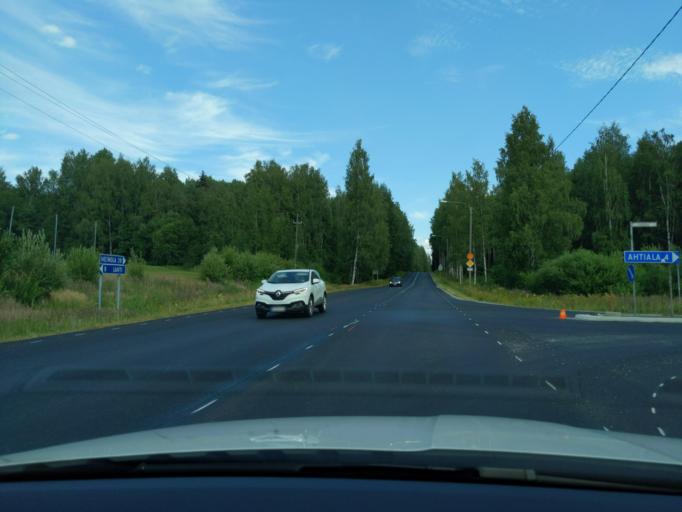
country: FI
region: Paijanne Tavastia
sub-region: Lahti
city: Lahti
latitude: 61.0270
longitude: 25.7309
